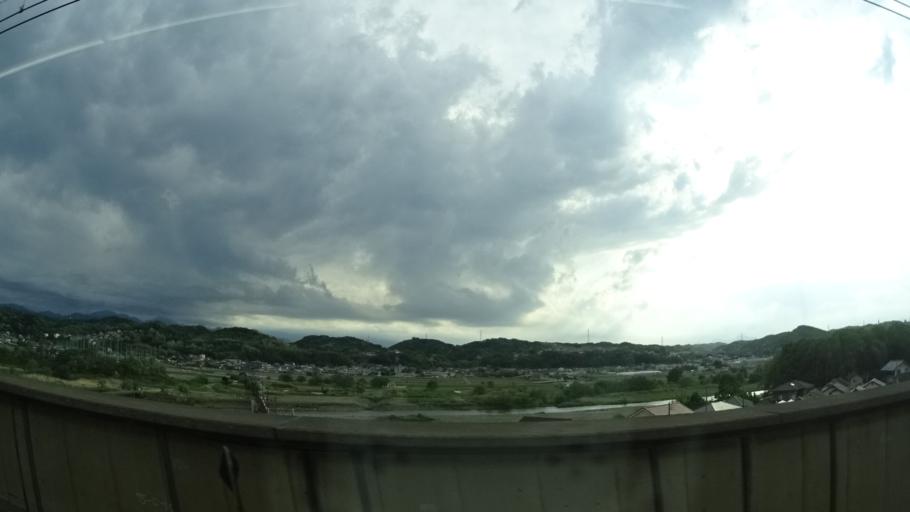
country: JP
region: Gunma
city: Takasaki
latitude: 36.3037
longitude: 139.0181
